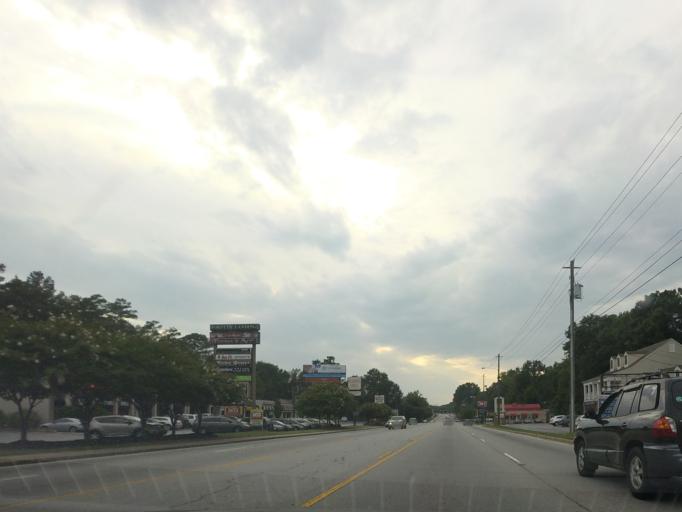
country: US
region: Georgia
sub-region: Bibb County
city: Macon
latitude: 32.8716
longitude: -83.7042
